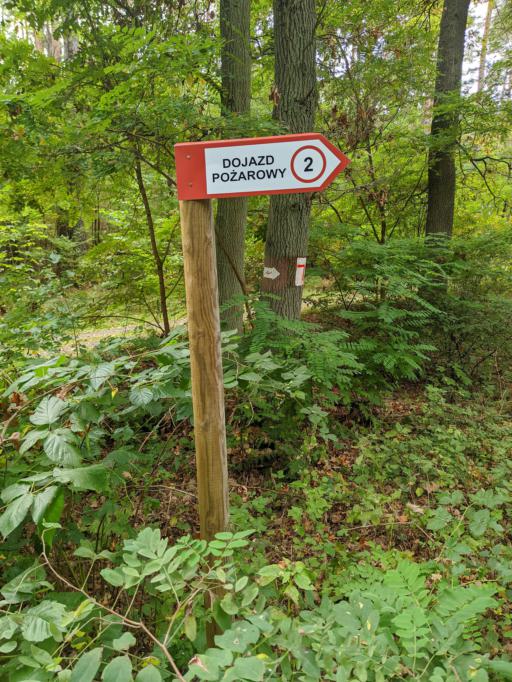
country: PL
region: Lubusz
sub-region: Zielona Gora
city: Zielona Gora
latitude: 51.9145
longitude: 15.4814
